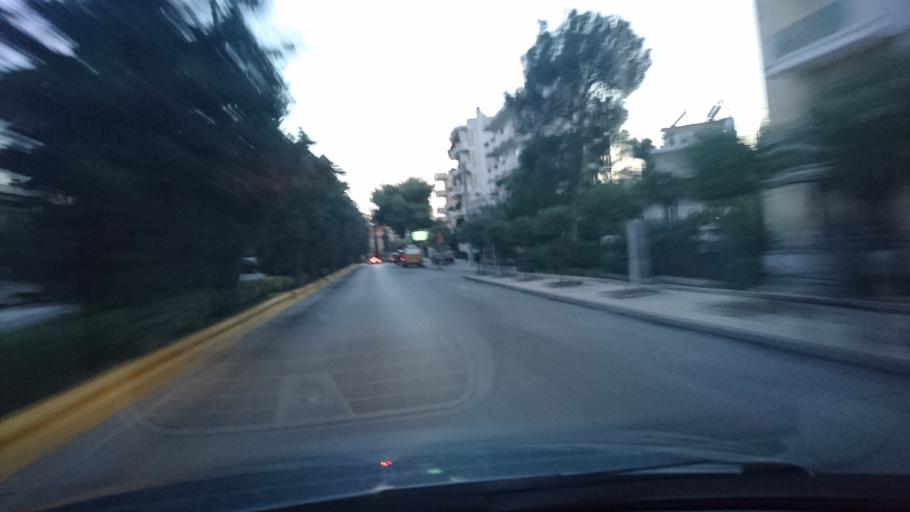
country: GR
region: Attica
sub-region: Nomarchia Athinas
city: Ilioupoli
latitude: 37.9259
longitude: 23.7524
